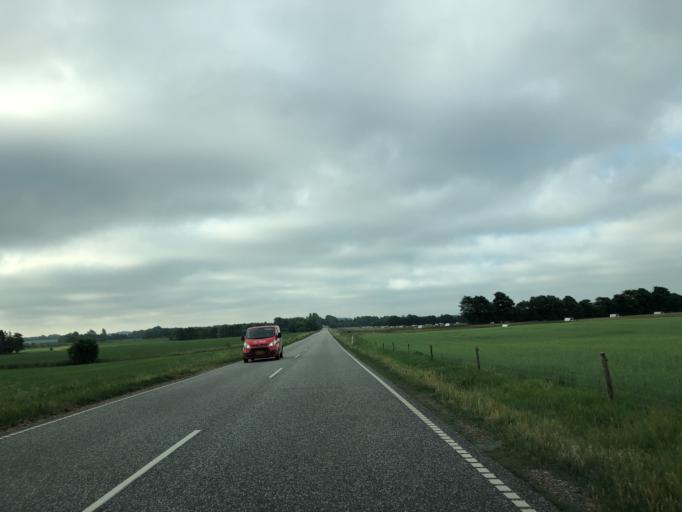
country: DK
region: South Denmark
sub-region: Vejle Kommune
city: Give
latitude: 55.8756
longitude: 9.2322
